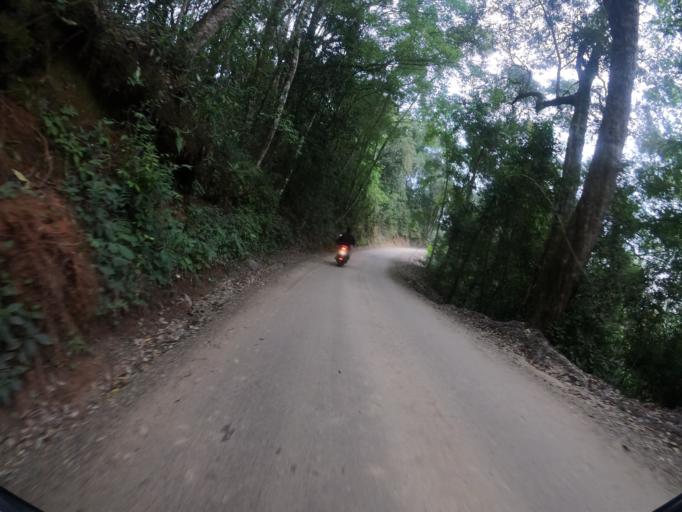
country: TH
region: Chiang Mai
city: Chiang Mai
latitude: 18.8162
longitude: 98.8945
